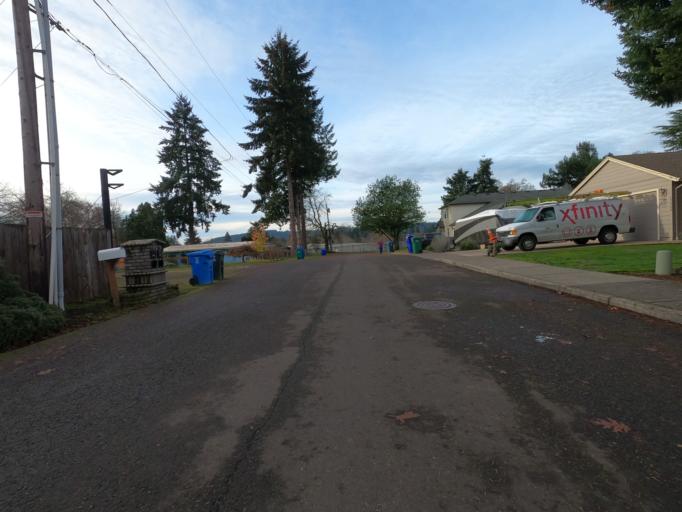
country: US
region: Oregon
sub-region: Clackamas County
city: Jennings Lodge
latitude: 45.3944
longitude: -122.6019
